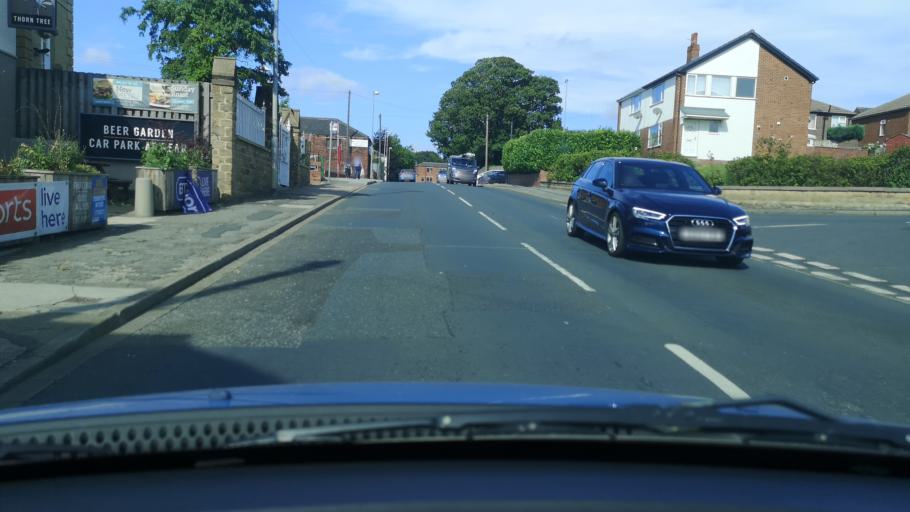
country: GB
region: England
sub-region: City and Borough of Wakefield
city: Ossett
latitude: 53.6767
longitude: -1.5800
